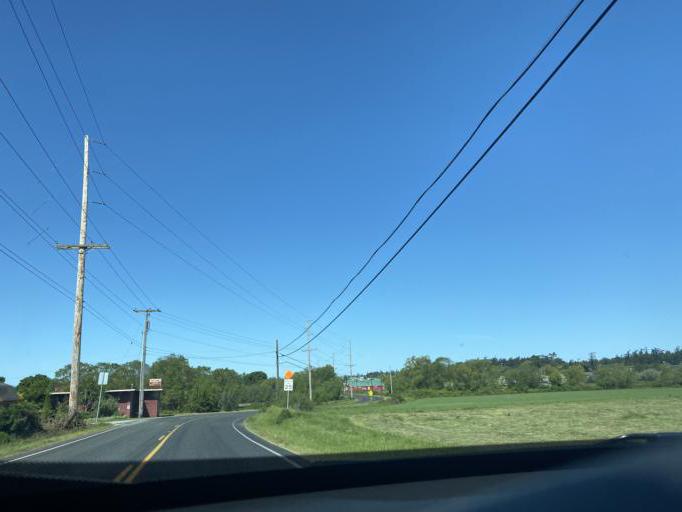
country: US
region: Washington
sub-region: Island County
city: Coupeville
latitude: 48.2067
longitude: -122.6800
